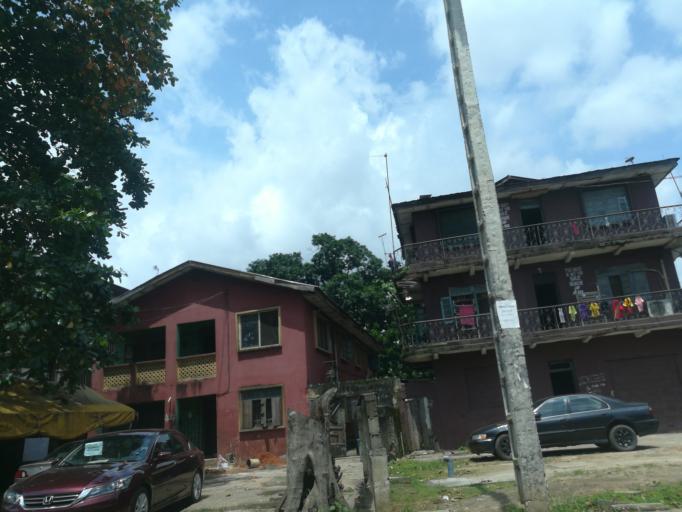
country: NG
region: Lagos
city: Somolu
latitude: 6.5394
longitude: 3.3634
